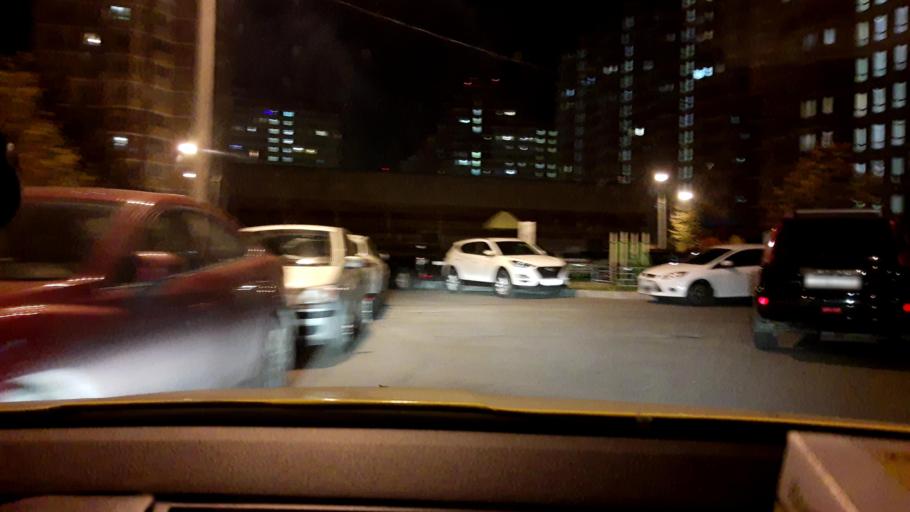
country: RU
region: Moskovskaya
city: Moskovskiy
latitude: 55.5978
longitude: 37.3424
